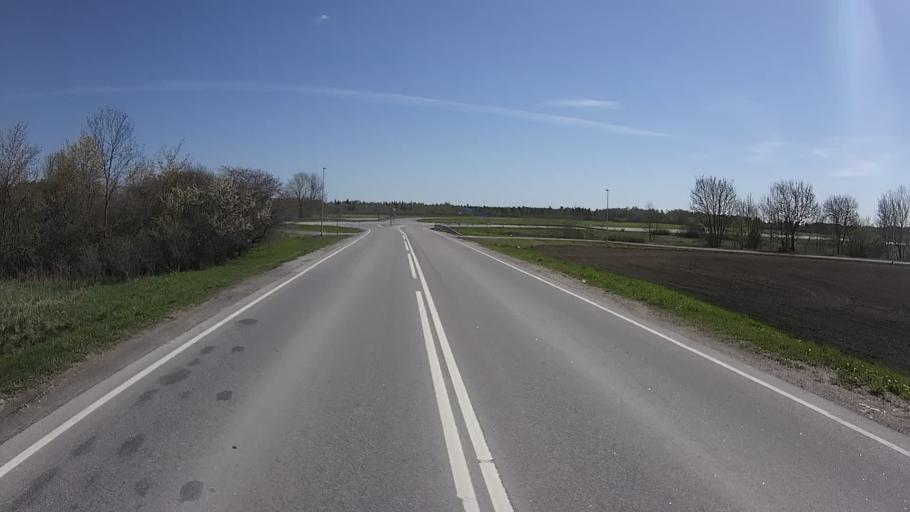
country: EE
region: Harju
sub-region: Keila linn
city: Keila
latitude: 59.2938
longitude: 24.3397
